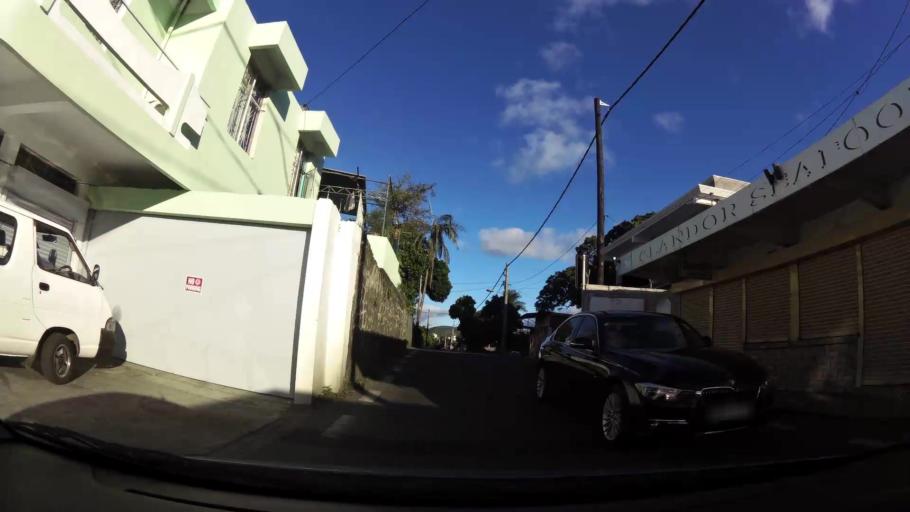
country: MU
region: Plaines Wilhems
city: Quatre Bornes
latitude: -20.2465
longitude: 57.4681
